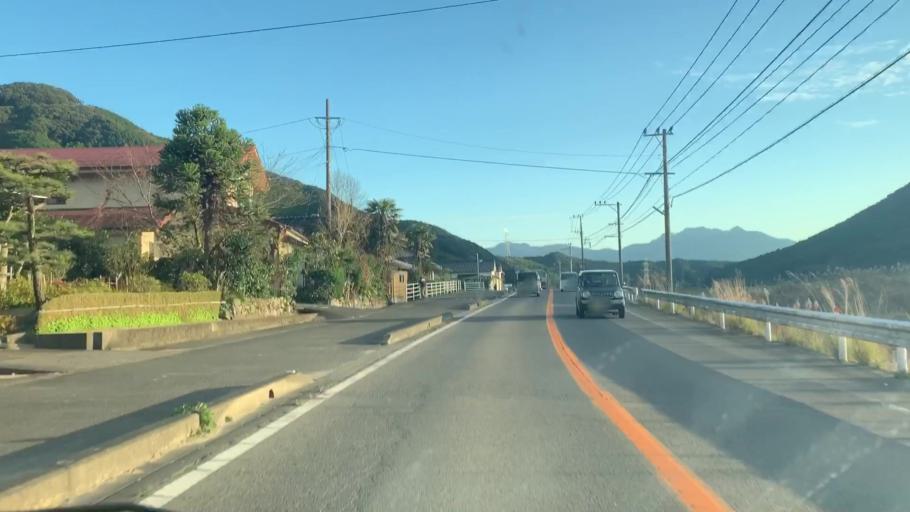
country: JP
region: Saga Prefecture
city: Karatsu
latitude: 33.3725
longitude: 130.0025
